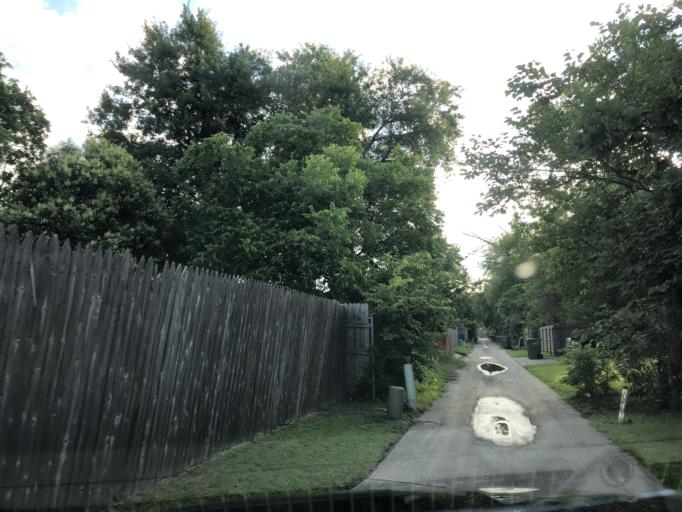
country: US
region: Texas
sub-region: Dallas County
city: Garland
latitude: 32.8484
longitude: -96.6232
